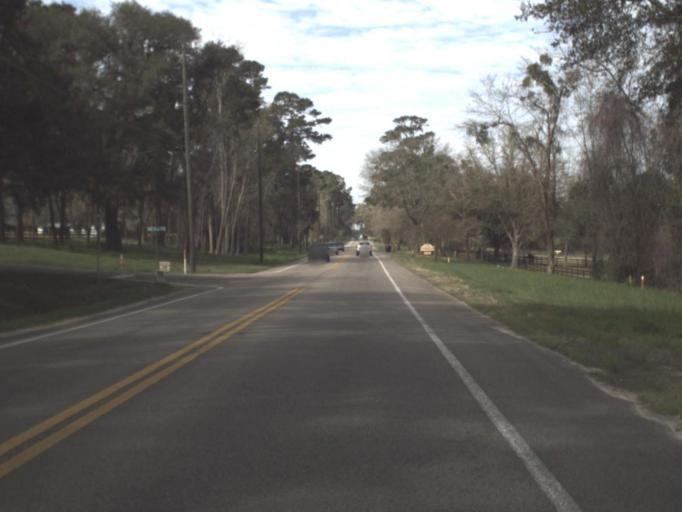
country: US
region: Florida
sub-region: Leon County
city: Tallahassee
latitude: 30.4898
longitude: -84.1372
